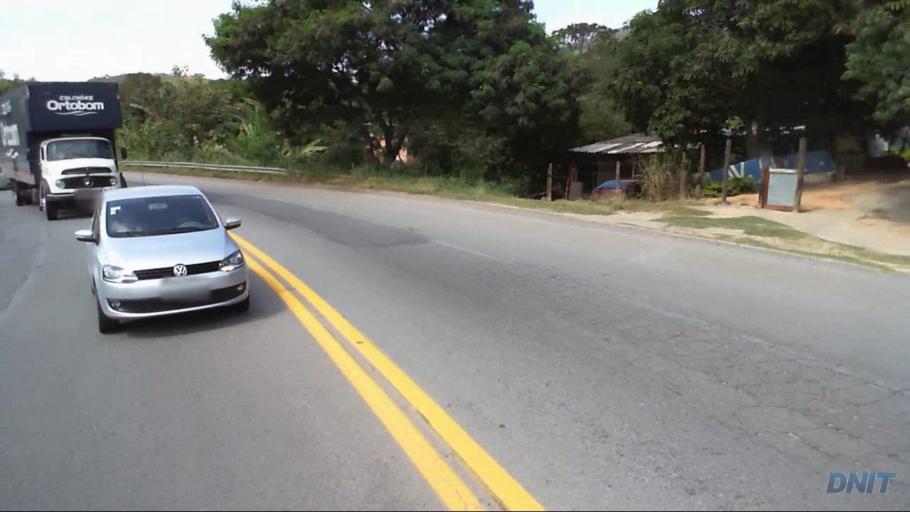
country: BR
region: Minas Gerais
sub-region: Santa Luzia
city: Santa Luzia
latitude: -19.8159
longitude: -43.8023
